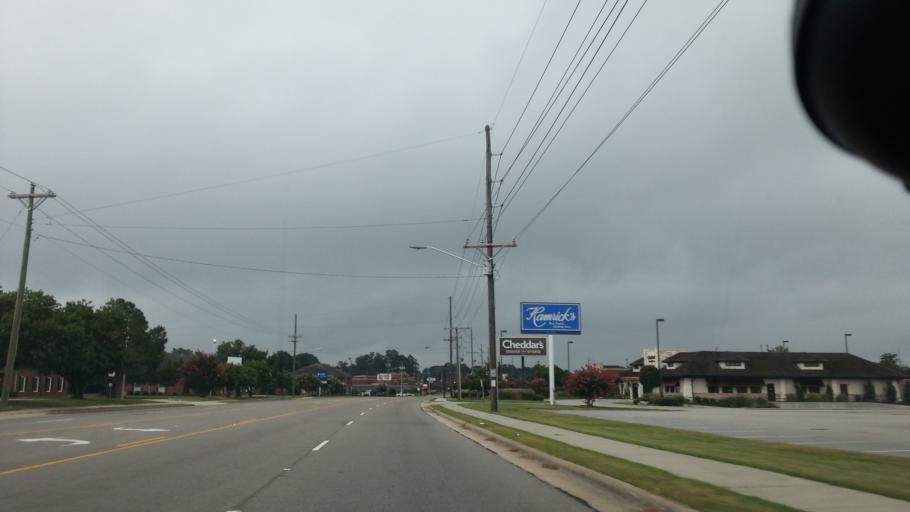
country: US
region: North Carolina
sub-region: Cumberland County
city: Fayetteville
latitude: 35.0714
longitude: -78.9519
